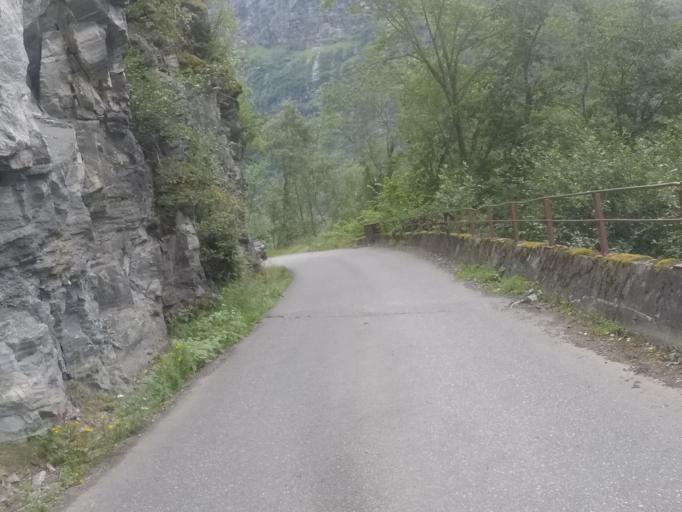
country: NO
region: Sogn og Fjordane
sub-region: Stryn
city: Stryn
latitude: 61.7890
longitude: 6.9986
